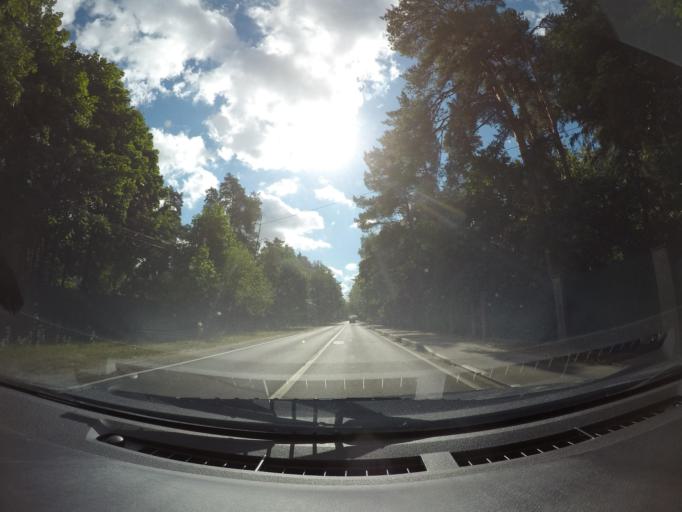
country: RU
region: Moskovskaya
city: Il'inskiy
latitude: 55.6192
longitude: 38.1184
